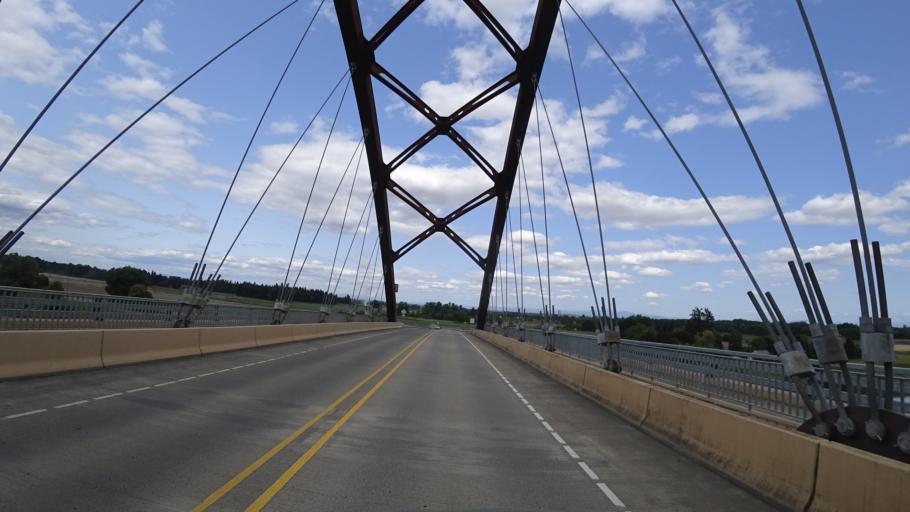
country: US
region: Oregon
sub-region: Washington County
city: Bethany
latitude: 45.6277
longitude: -122.8165
